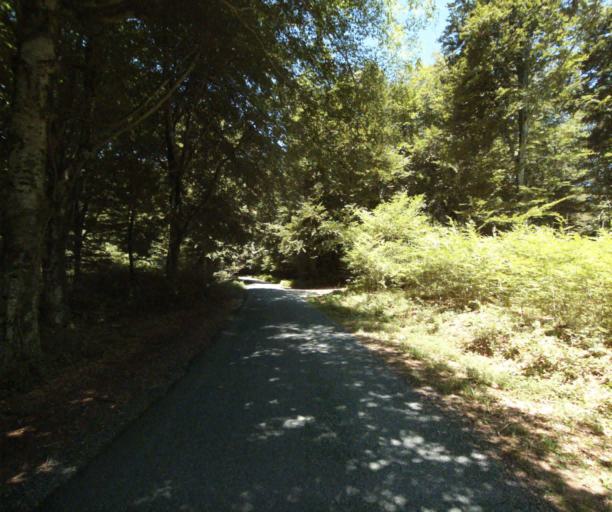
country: FR
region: Midi-Pyrenees
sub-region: Departement du Tarn
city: Dourgne
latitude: 43.4194
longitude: 2.1873
